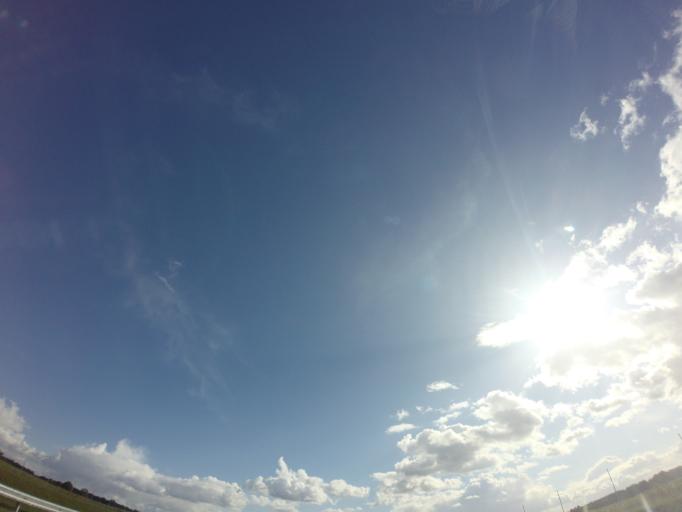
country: PL
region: Lubusz
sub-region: Powiat nowosolski
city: Nowe Miasteczko
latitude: 51.7010
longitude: 15.7534
